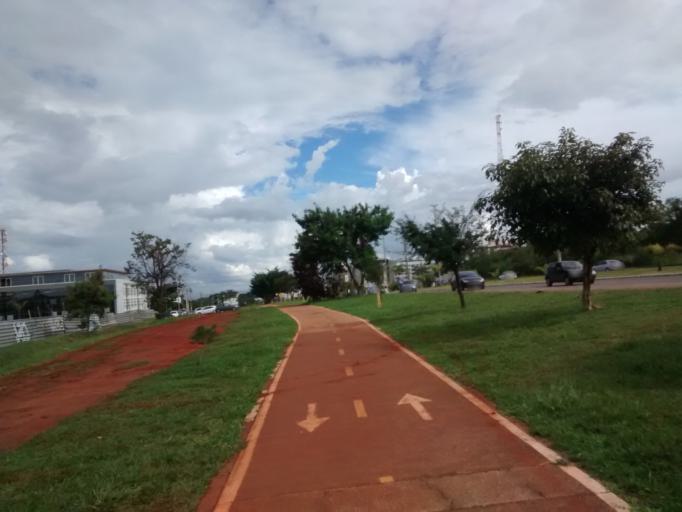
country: BR
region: Federal District
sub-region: Brasilia
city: Brasilia
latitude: -15.7854
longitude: -47.9137
